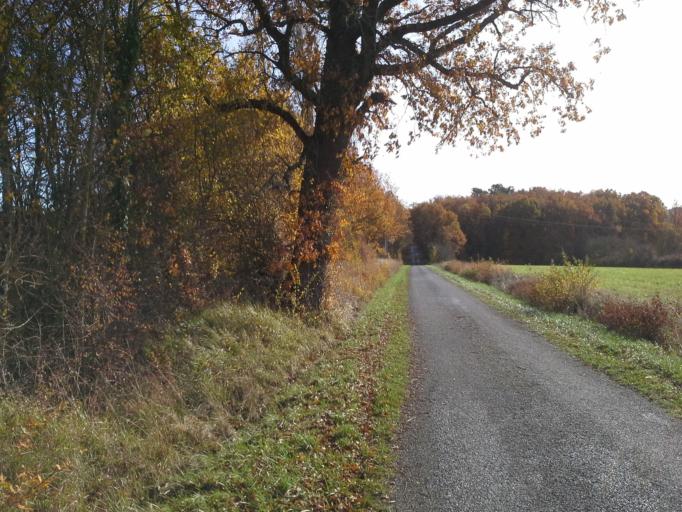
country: FR
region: Poitou-Charentes
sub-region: Departement de la Vienne
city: Pleumartin
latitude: 46.6416
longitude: 0.7602
